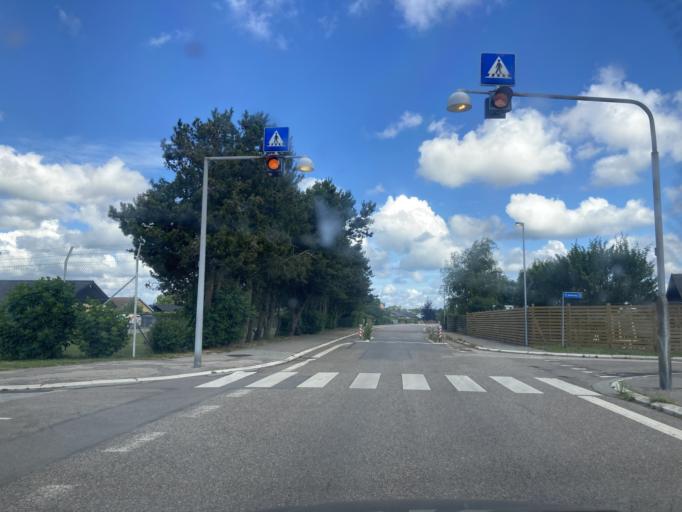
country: DK
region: Capital Region
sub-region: Halsnaes Kommune
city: Frederiksvaerk
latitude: 55.9852
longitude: 12.0111
